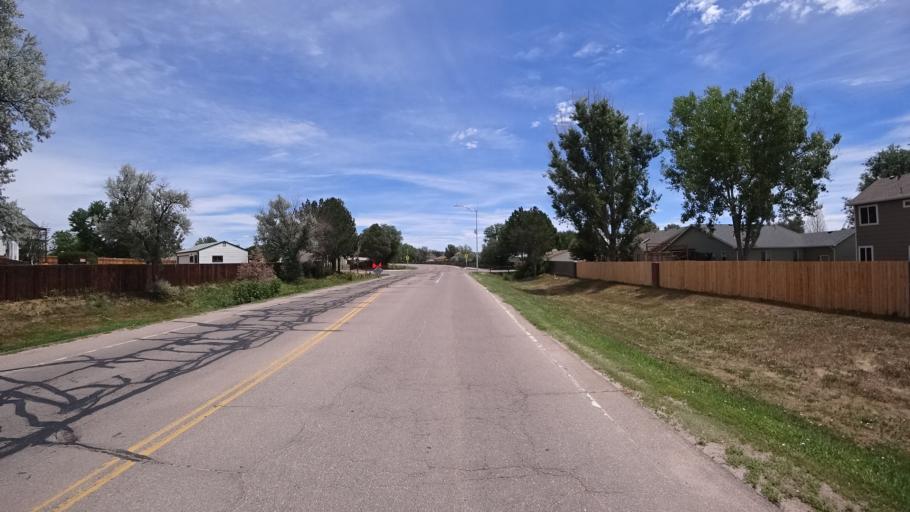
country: US
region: Colorado
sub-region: El Paso County
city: Fountain
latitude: 38.6685
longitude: -104.6775
